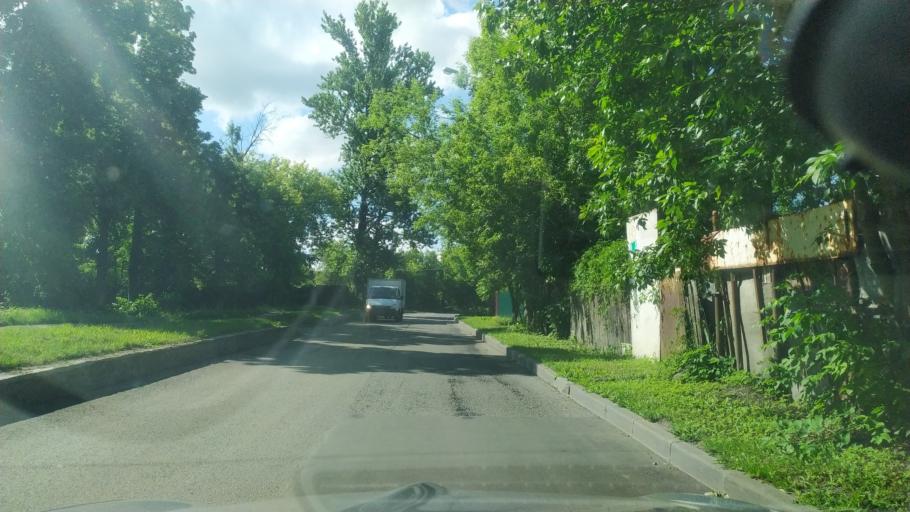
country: RU
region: Moscow
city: Vostochnyy
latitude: 55.8150
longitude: 37.8657
